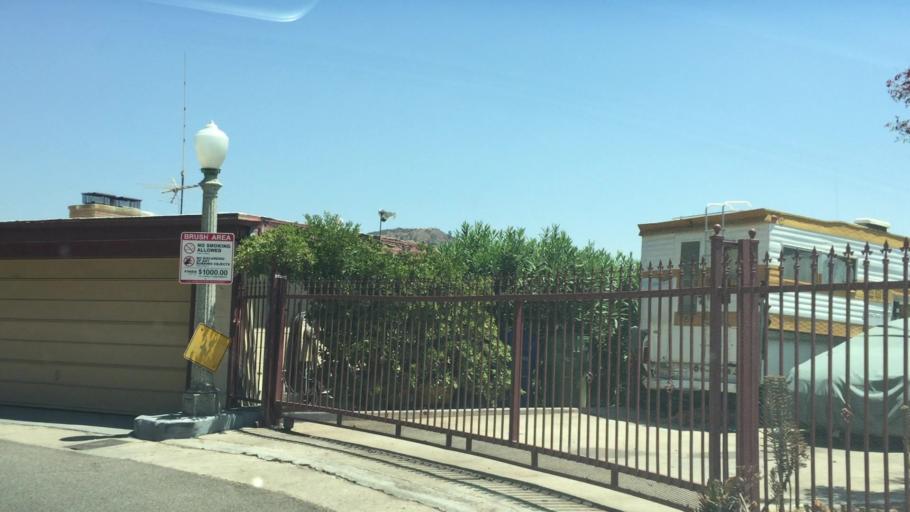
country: US
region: California
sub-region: Los Angeles County
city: Hollywood
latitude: 34.1259
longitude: -118.3202
